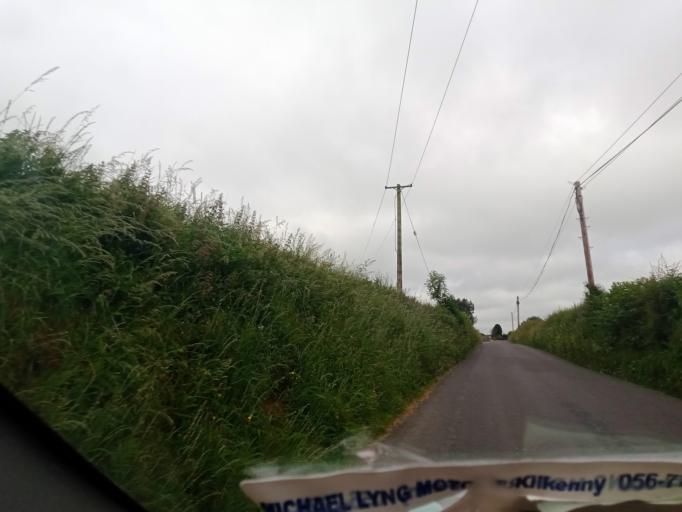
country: IE
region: Leinster
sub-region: Kilkenny
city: Ballyragget
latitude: 52.7508
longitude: -7.4367
